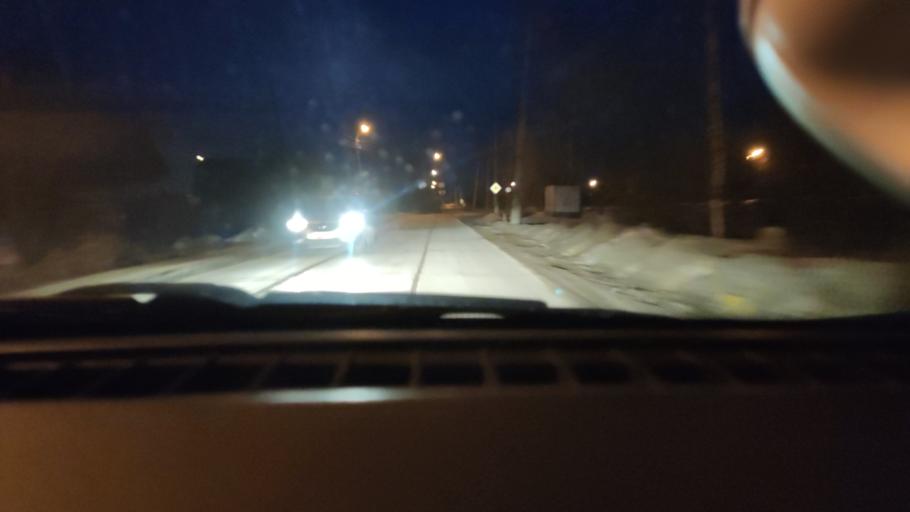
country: RU
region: Perm
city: Overyata
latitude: 58.0873
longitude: 55.8619
